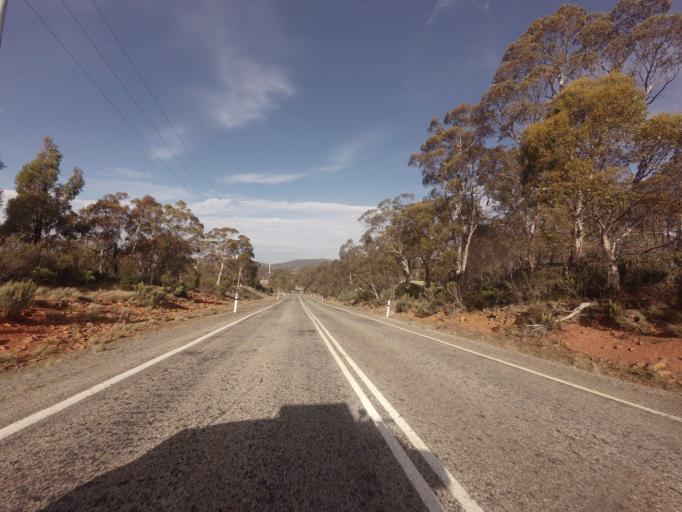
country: AU
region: Tasmania
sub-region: Meander Valley
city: Deloraine
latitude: -41.9917
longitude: 146.6998
